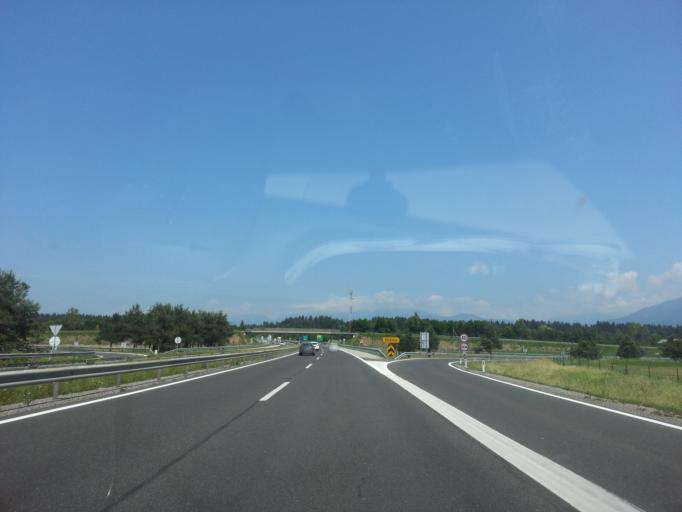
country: SI
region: Vodice
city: Vodice
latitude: 46.1818
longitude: 14.4845
